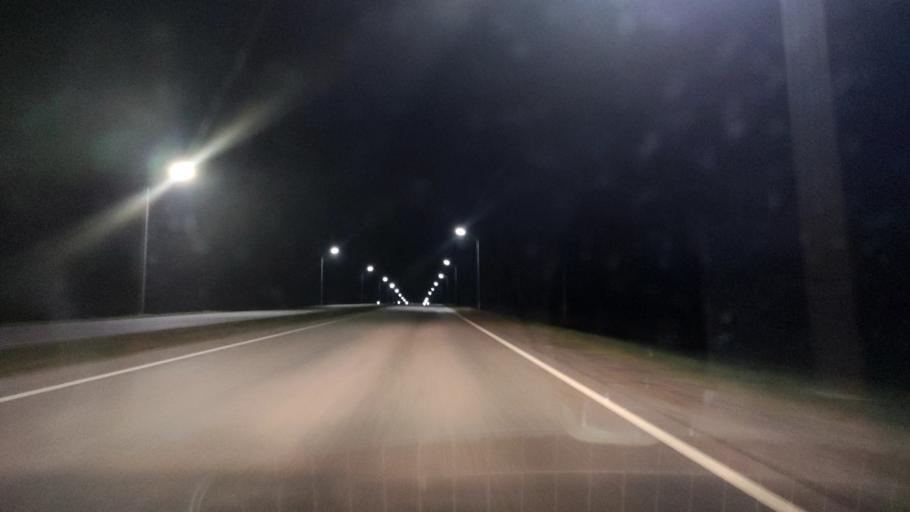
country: RU
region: Belgorod
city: Staryy Oskol
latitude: 51.3843
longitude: 37.8587
